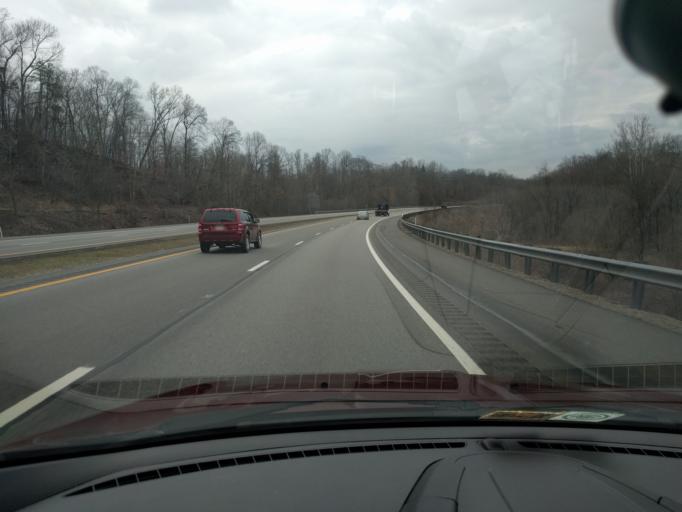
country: US
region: West Virginia
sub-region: Wood County
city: Boaz
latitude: 39.3362
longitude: -81.4625
